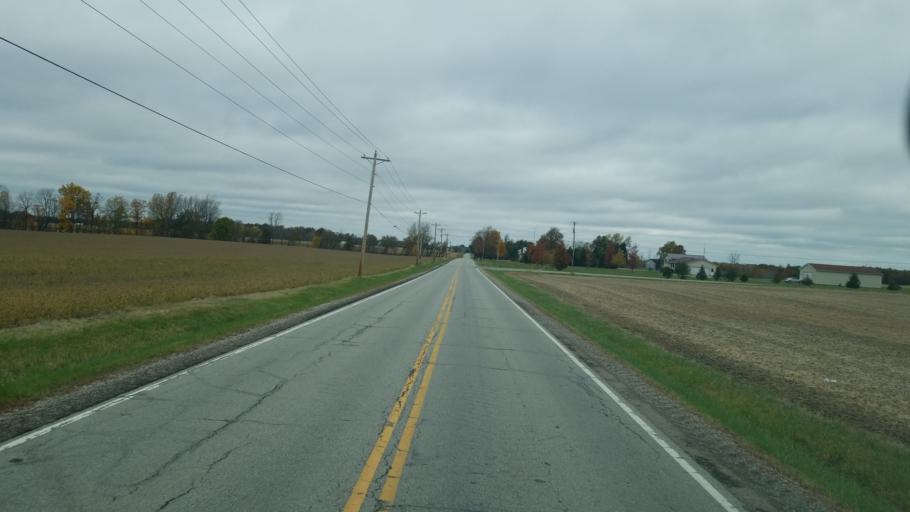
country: US
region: Ohio
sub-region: Huron County
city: Willard
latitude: 40.9812
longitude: -82.8533
